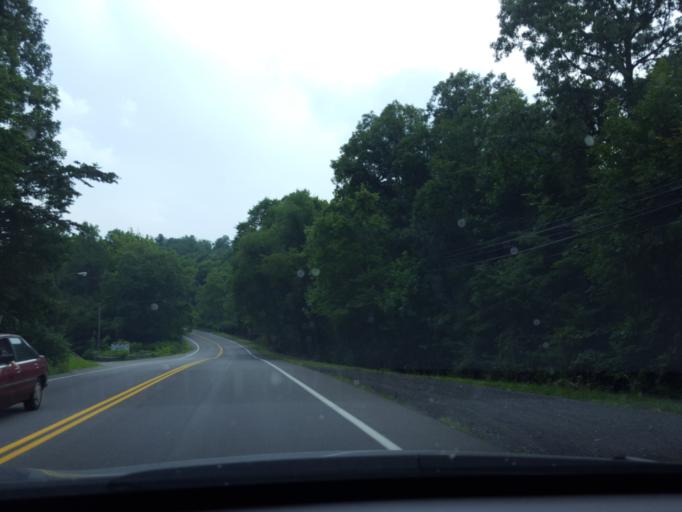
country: US
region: Virginia
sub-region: City of Waynesboro
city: Waynesboro
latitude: 38.0510
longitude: -78.8688
